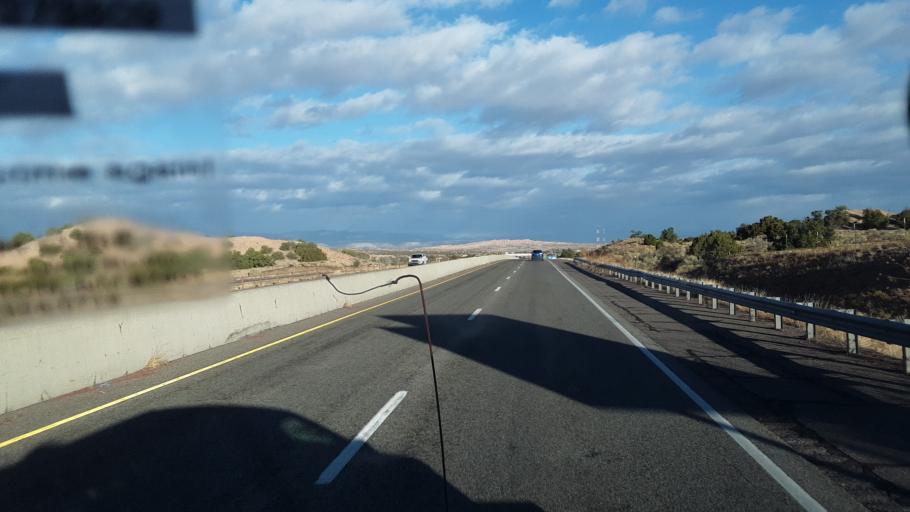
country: US
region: New Mexico
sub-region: Santa Fe County
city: Nambe
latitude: 35.8338
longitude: -105.9820
